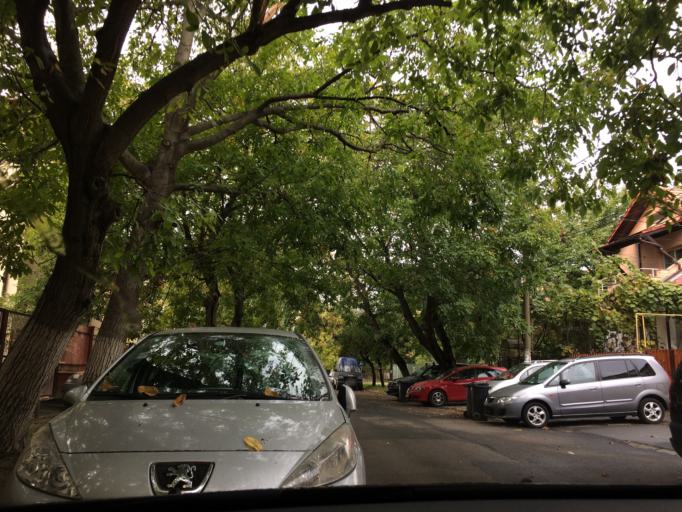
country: RO
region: Timis
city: Timisoara
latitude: 45.7601
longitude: 21.2136
